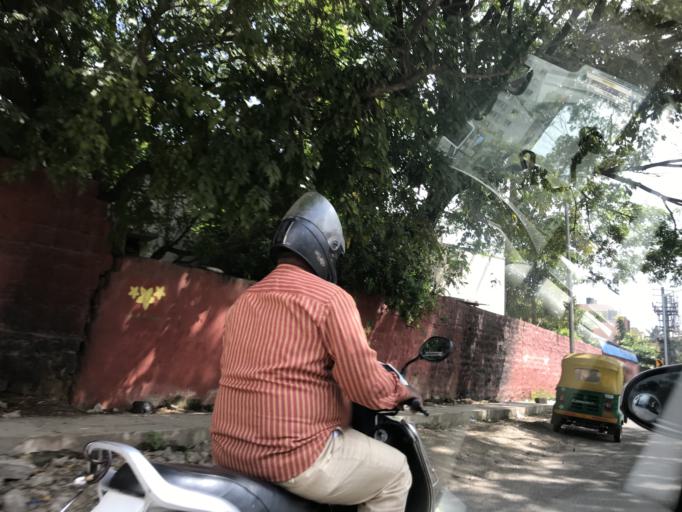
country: IN
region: Karnataka
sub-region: Bangalore Urban
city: Bangalore
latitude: 12.9791
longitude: 77.5645
